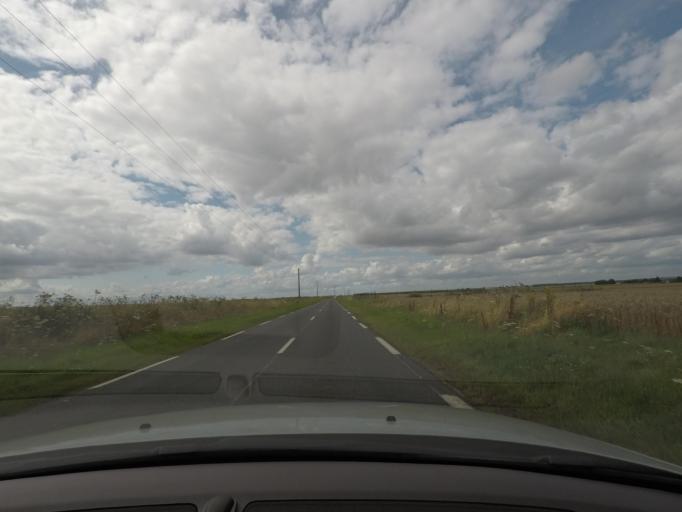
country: FR
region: Haute-Normandie
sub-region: Departement de l'Eure
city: Les Andelys
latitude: 49.2087
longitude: 1.4639
